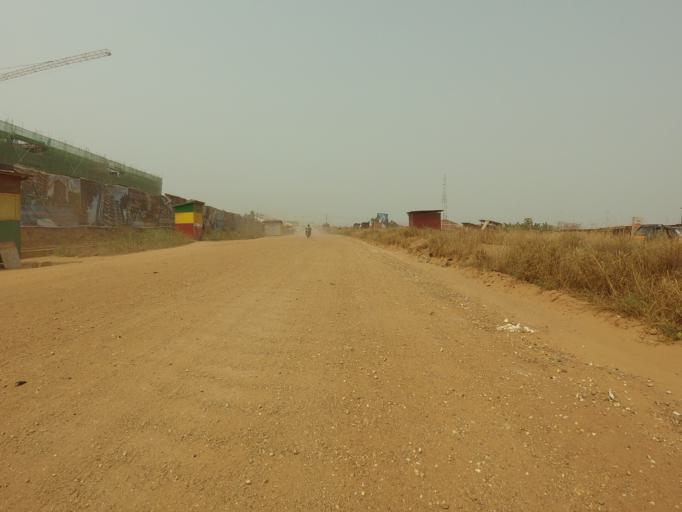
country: GH
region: Greater Accra
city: Medina Estates
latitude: 5.6347
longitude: -0.1253
